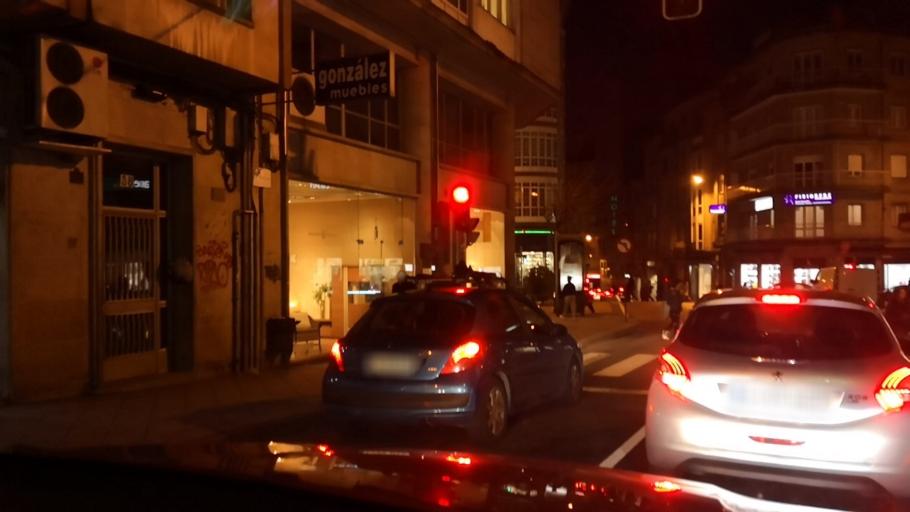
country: ES
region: Galicia
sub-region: Provincia de Ourense
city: Ourense
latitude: 42.3422
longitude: -7.8621
